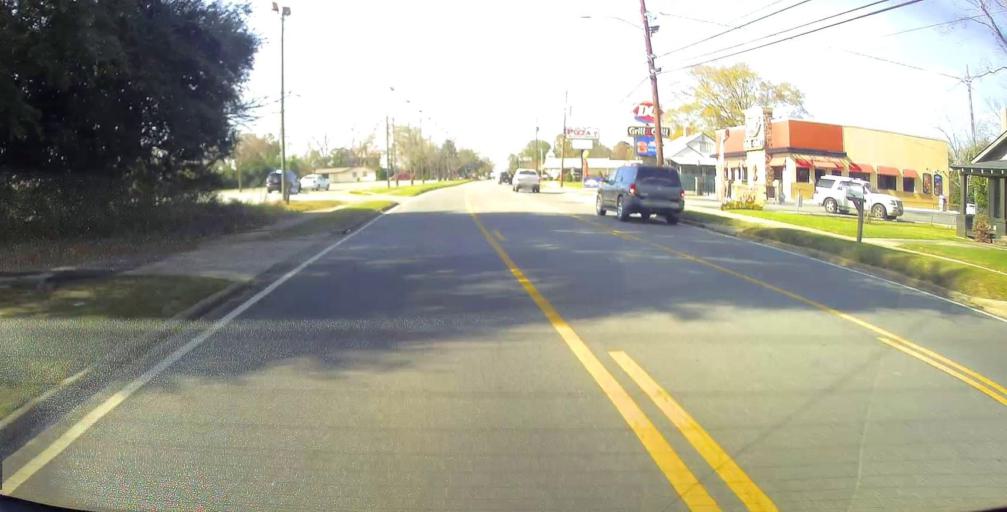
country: US
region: Georgia
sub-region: Dodge County
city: Eastman
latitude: 32.1861
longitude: -83.1713
